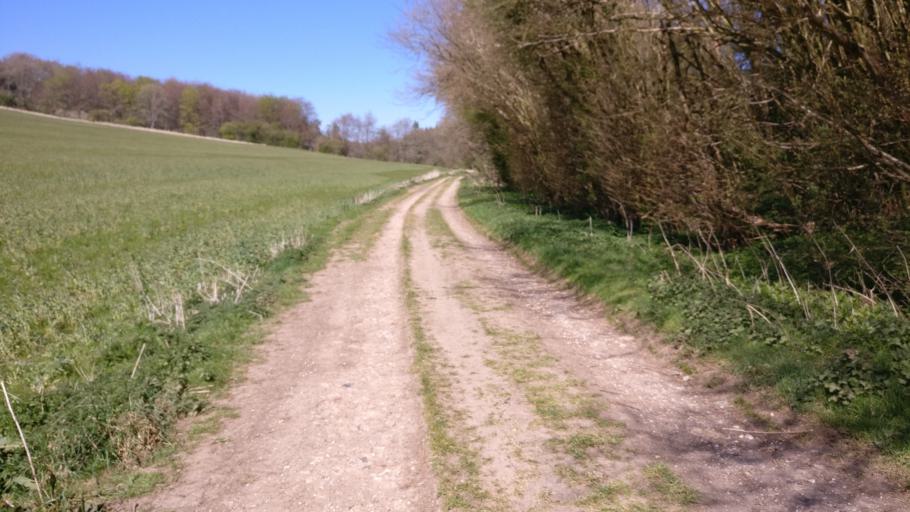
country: GB
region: England
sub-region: Hampshire
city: Basingstoke
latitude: 51.1947
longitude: -1.1121
